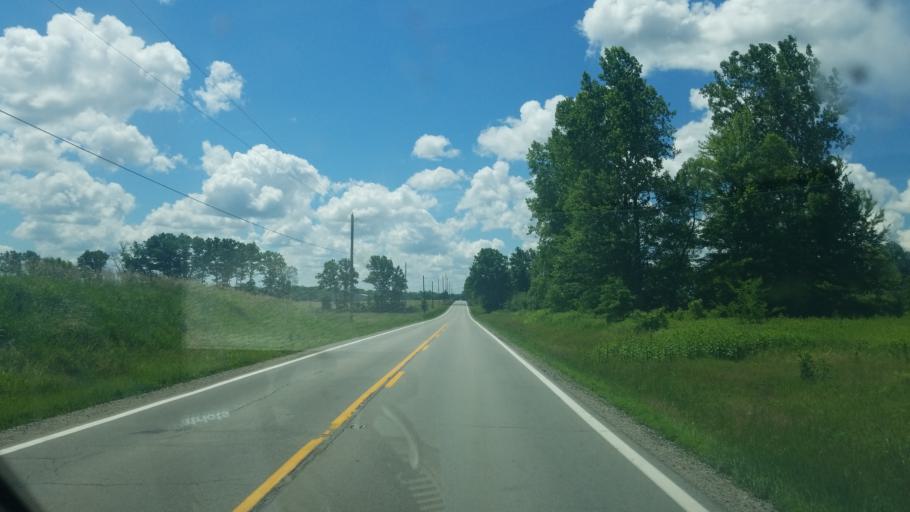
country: US
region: Ohio
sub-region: Huron County
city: New London
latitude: 41.1498
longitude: -82.4101
